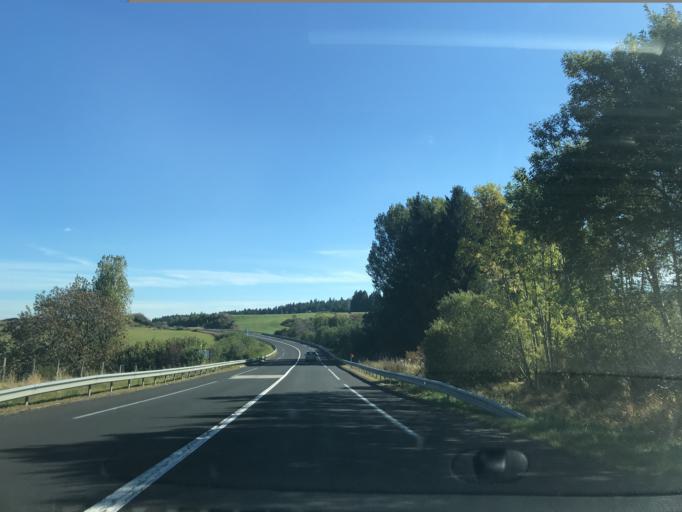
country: FR
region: Auvergne
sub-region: Departement du Puy-de-Dome
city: La Bourboule
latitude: 45.6603
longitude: 2.7659
